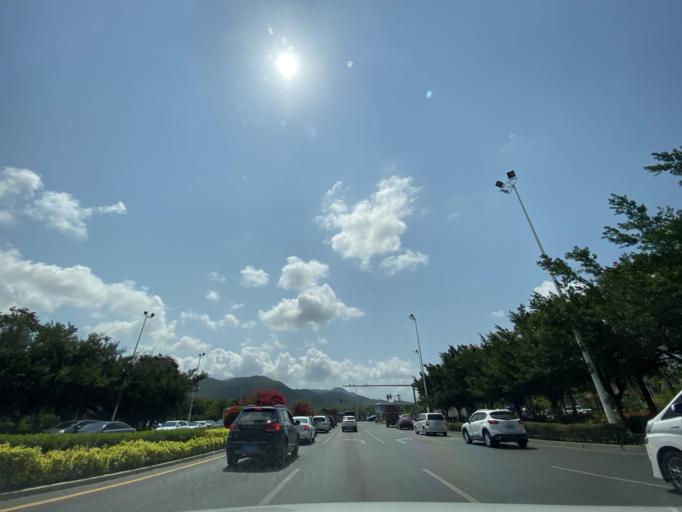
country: CN
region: Hainan
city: Tiandu
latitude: 18.2935
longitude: 109.5291
